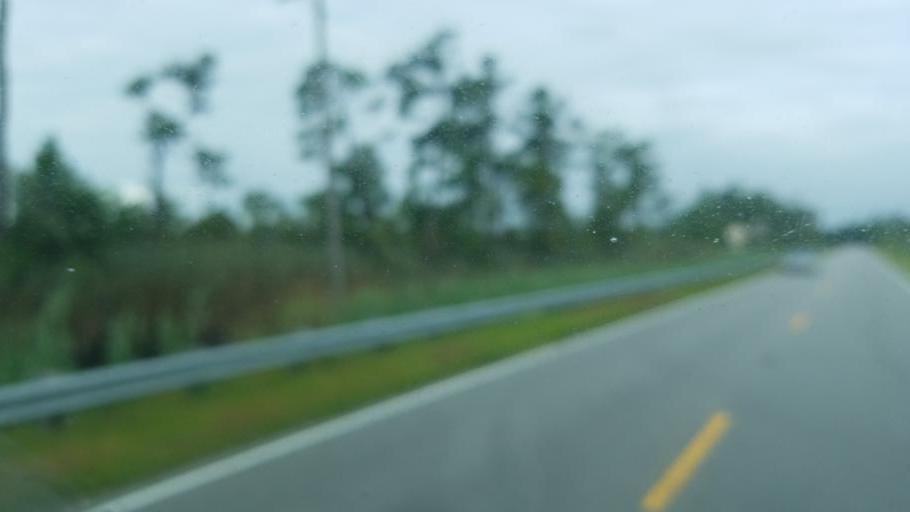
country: US
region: North Carolina
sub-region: Tyrrell County
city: Columbia
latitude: 35.9056
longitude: -76.0306
